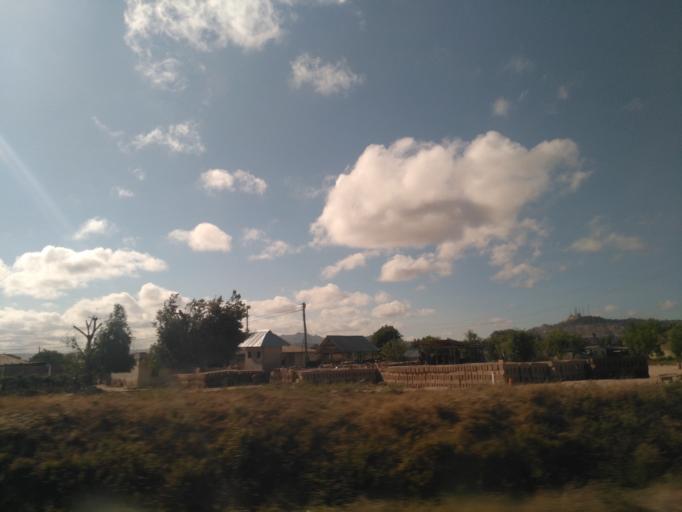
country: TZ
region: Dodoma
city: Dodoma
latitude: -6.1793
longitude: 35.7341
